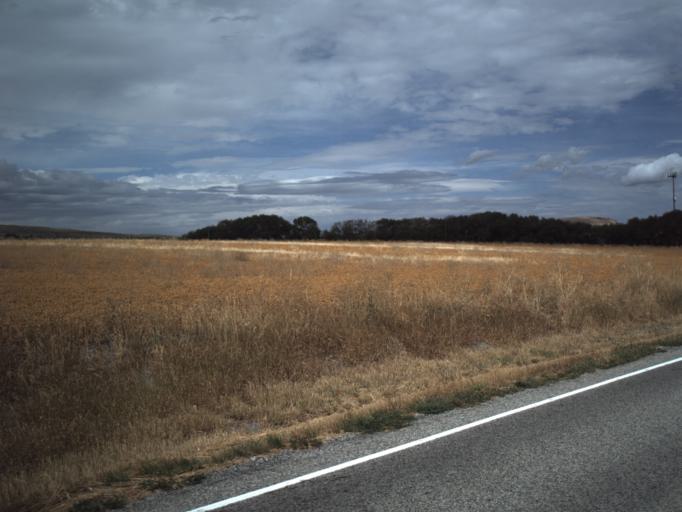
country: US
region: Utah
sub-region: Cache County
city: Mendon
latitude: 41.7395
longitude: -111.9792
